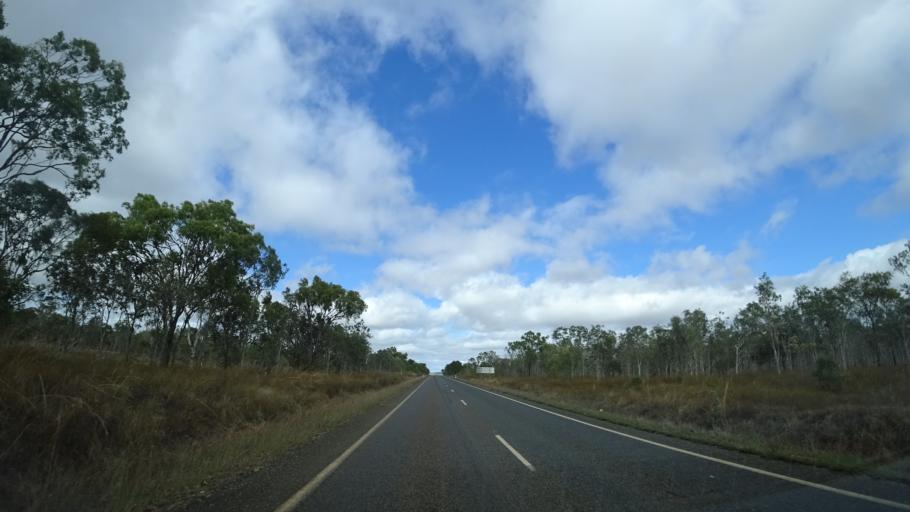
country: AU
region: Queensland
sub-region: Cook
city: Cooktown
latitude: -15.8795
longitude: 144.8600
